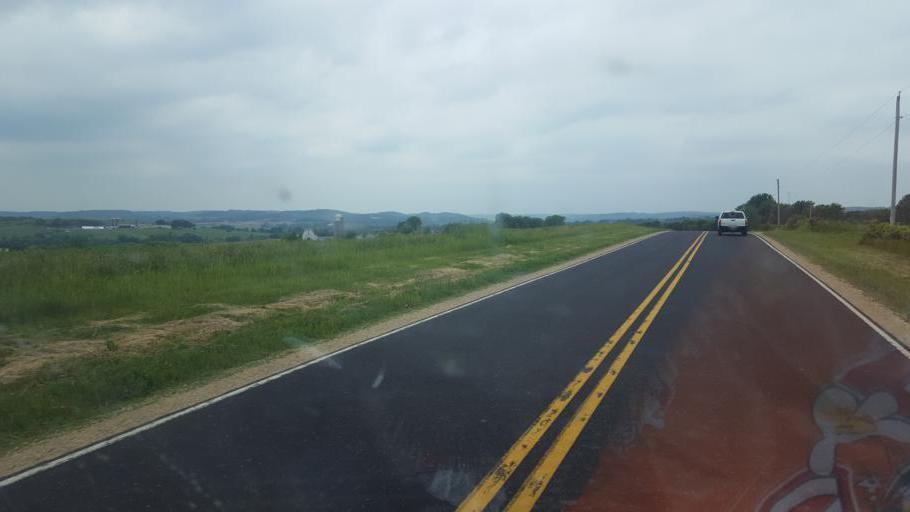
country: US
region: Wisconsin
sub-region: Vernon County
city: Hillsboro
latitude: 43.6511
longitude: -90.3182
